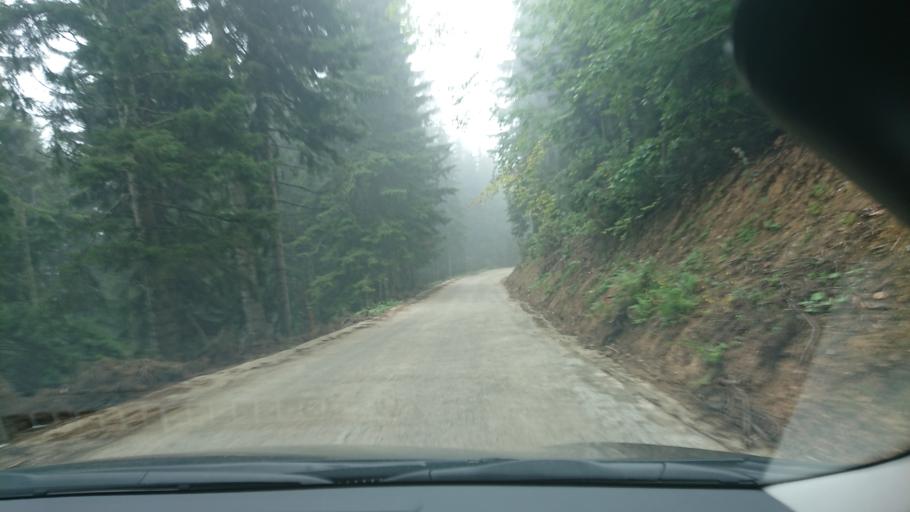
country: TR
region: Gumushane
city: Kurtun
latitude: 40.6648
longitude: 39.0161
